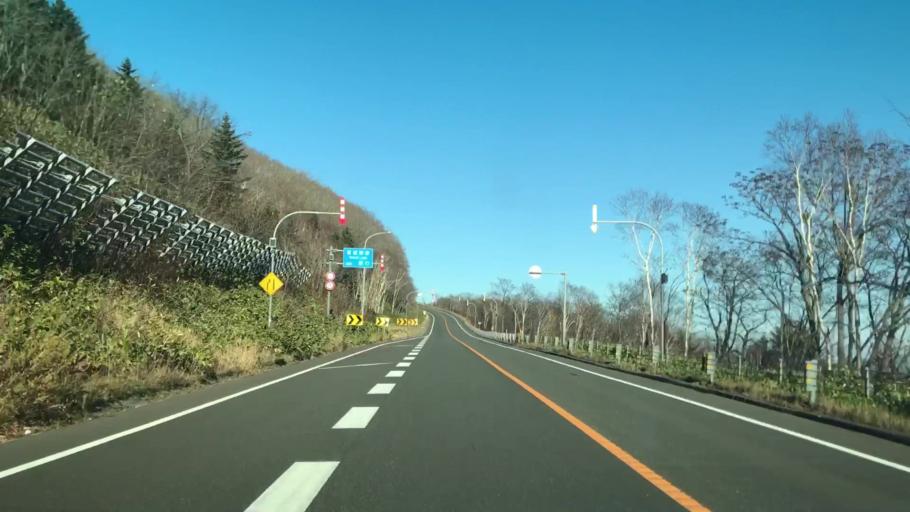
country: JP
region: Hokkaido
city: Otofuke
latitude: 42.9650
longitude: 142.7933
